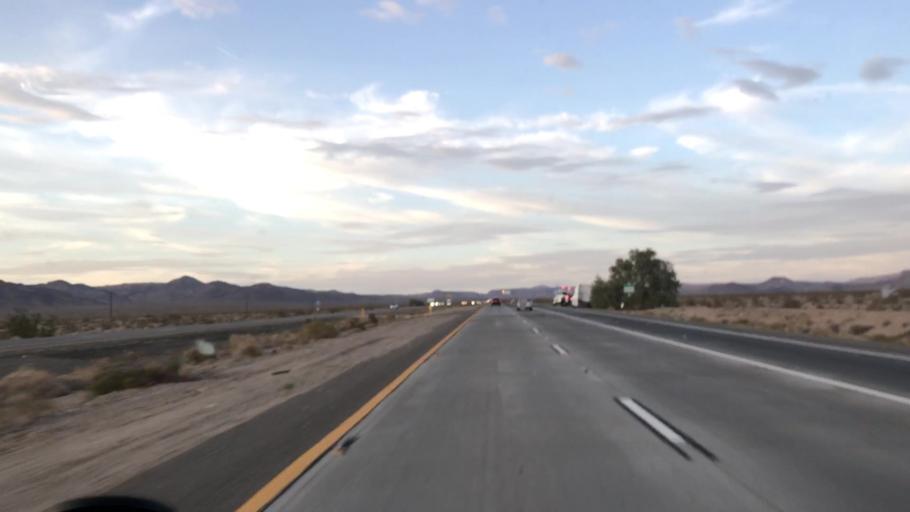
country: US
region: Nevada
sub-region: Clark County
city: Sandy Valley
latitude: 35.3111
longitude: -116.0029
